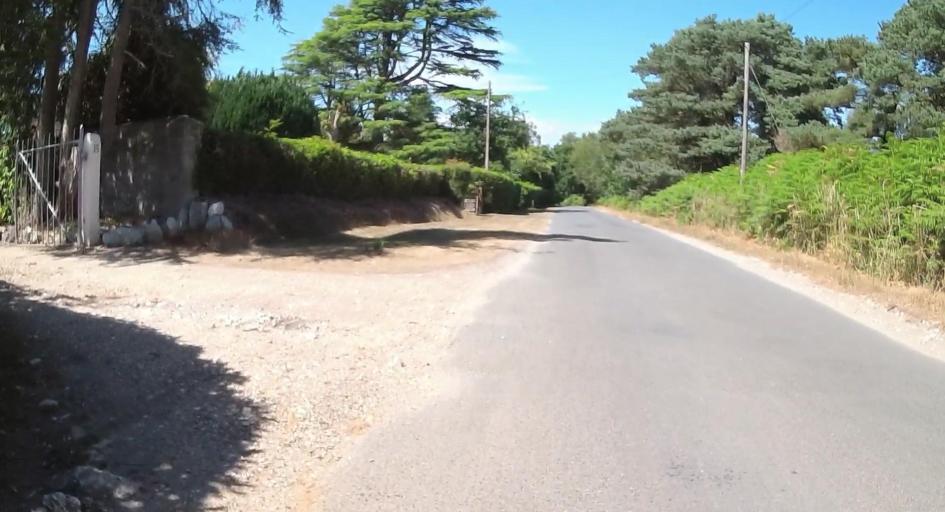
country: GB
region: England
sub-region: Dorset
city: Bovington Camp
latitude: 50.6940
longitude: -2.3010
